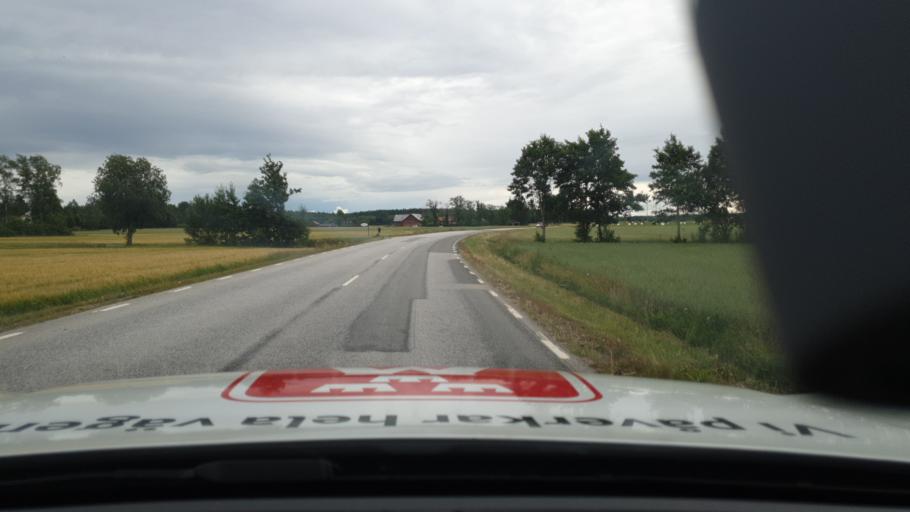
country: SE
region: Vaestra Goetaland
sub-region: Toreboda Kommun
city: Toereboda
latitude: 58.6991
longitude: 14.1343
